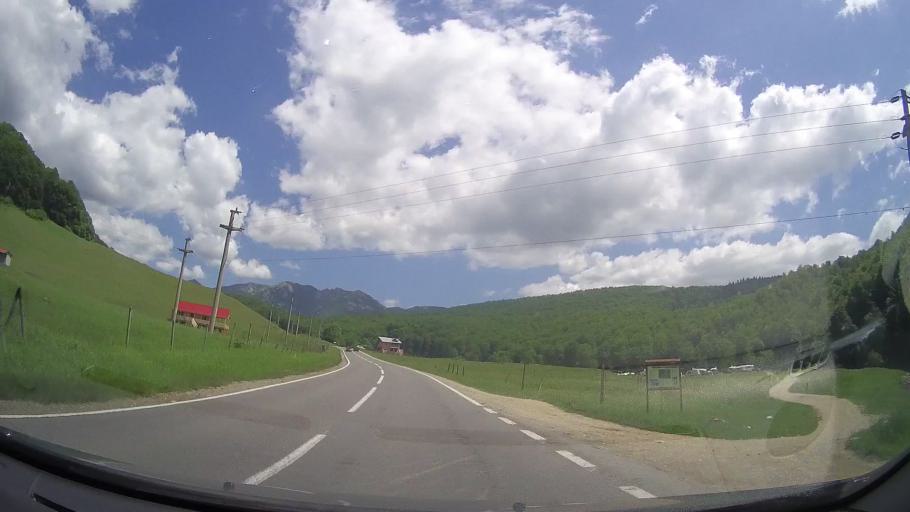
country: RO
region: Prahova
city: Maneciu
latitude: 45.4376
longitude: 25.9371
